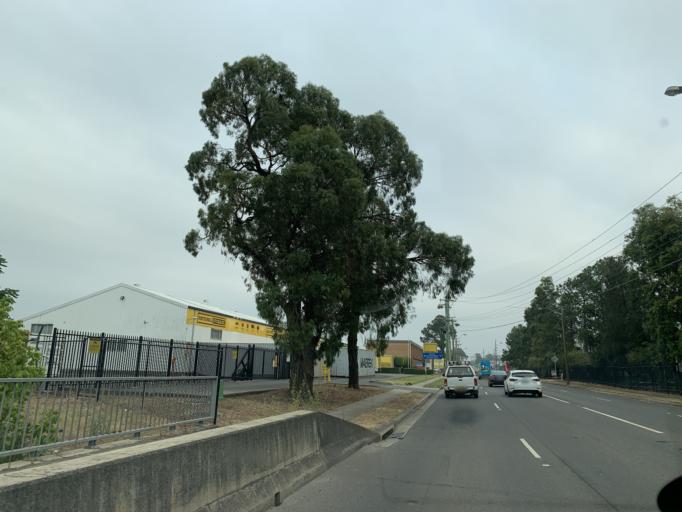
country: AU
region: New South Wales
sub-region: Holroyd
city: Girraween
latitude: -33.7762
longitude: 150.9449
